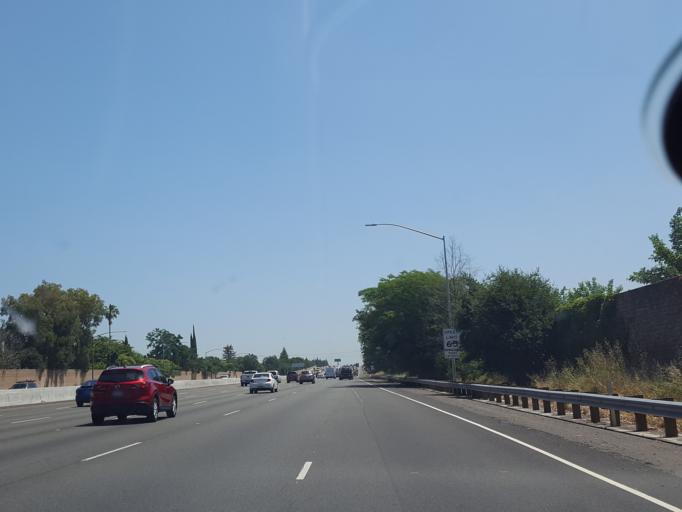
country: US
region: California
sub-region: Sacramento County
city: Rosemont
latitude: 38.5594
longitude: -121.3711
